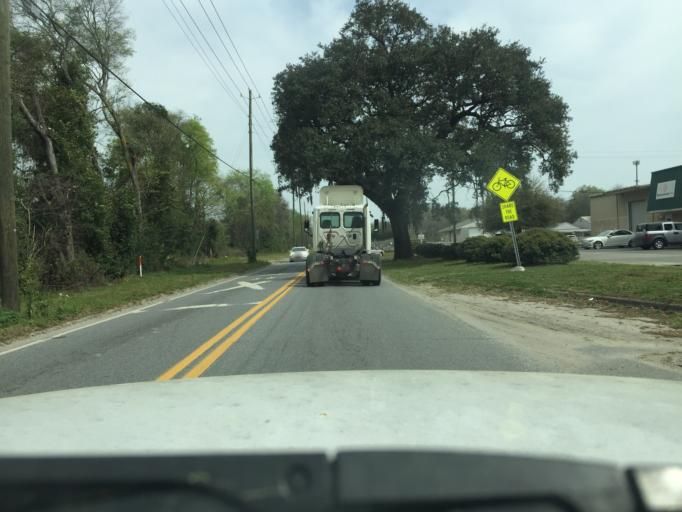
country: US
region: Georgia
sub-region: Chatham County
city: Savannah
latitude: 32.0804
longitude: -81.1164
